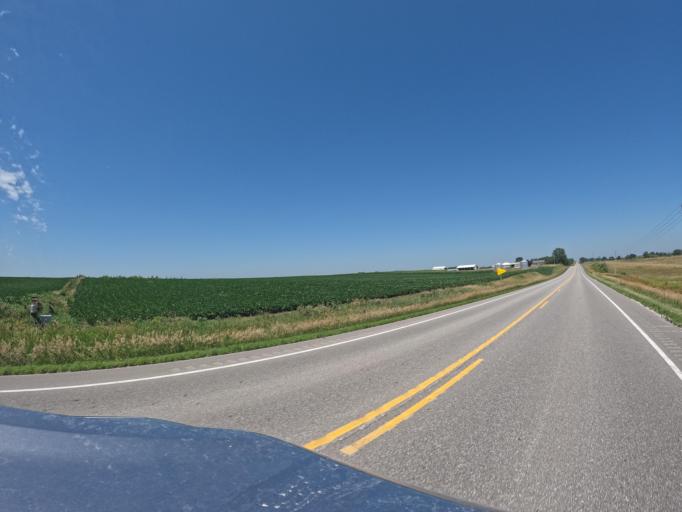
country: US
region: Iowa
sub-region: Keokuk County
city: Sigourney
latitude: 41.4559
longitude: -92.3551
